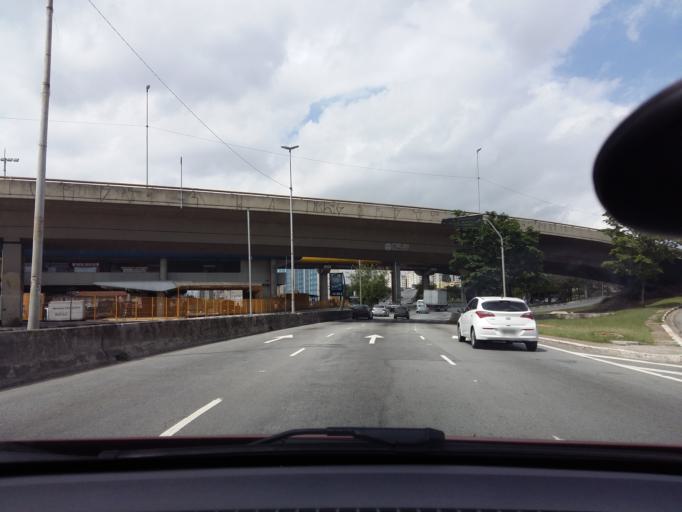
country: BR
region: Sao Paulo
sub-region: Sao Caetano Do Sul
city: Sao Caetano do Sul
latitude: -23.6042
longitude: -46.6031
